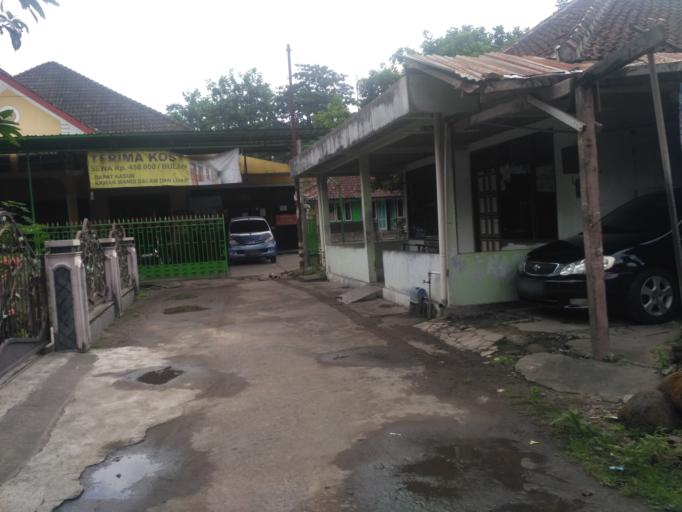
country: ID
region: Daerah Istimewa Yogyakarta
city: Melati
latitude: -7.7526
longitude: 110.3592
